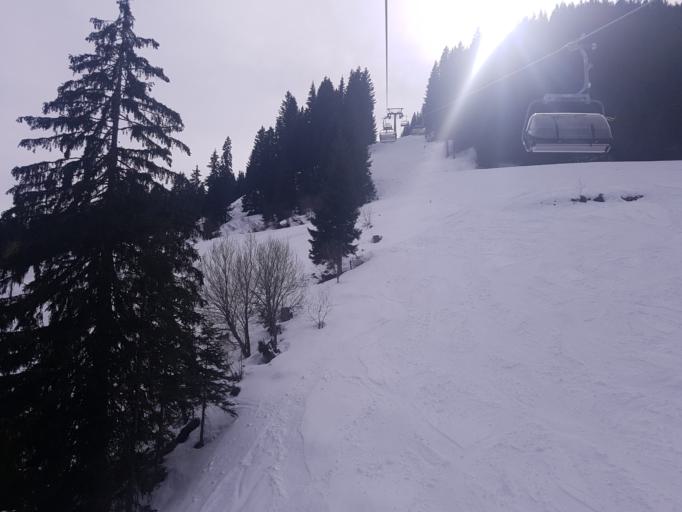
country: AT
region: Tyrol
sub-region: Politischer Bezirk Kufstein
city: Worgl
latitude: 47.4357
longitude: 12.0837
